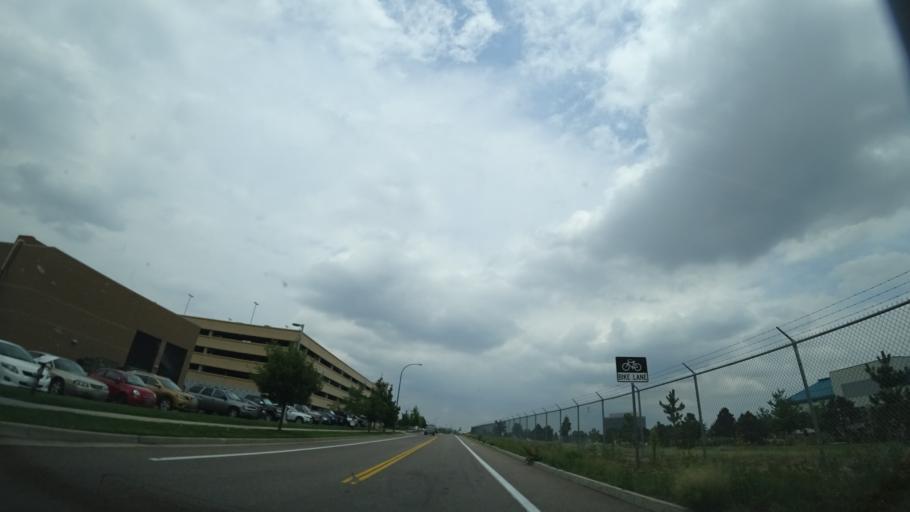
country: US
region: Colorado
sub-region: Jefferson County
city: Lakewood
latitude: 39.7161
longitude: -105.1274
